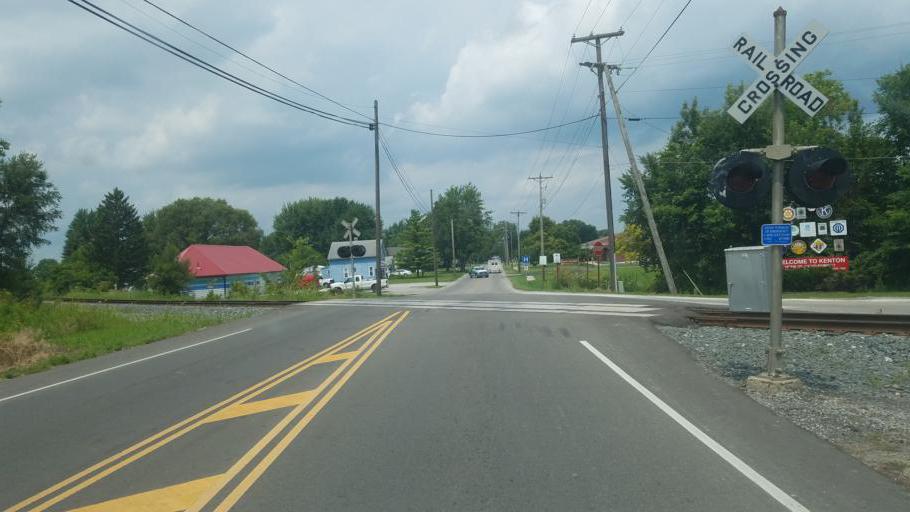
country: US
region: Ohio
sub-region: Hardin County
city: Kenton
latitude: 40.6349
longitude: -83.6026
